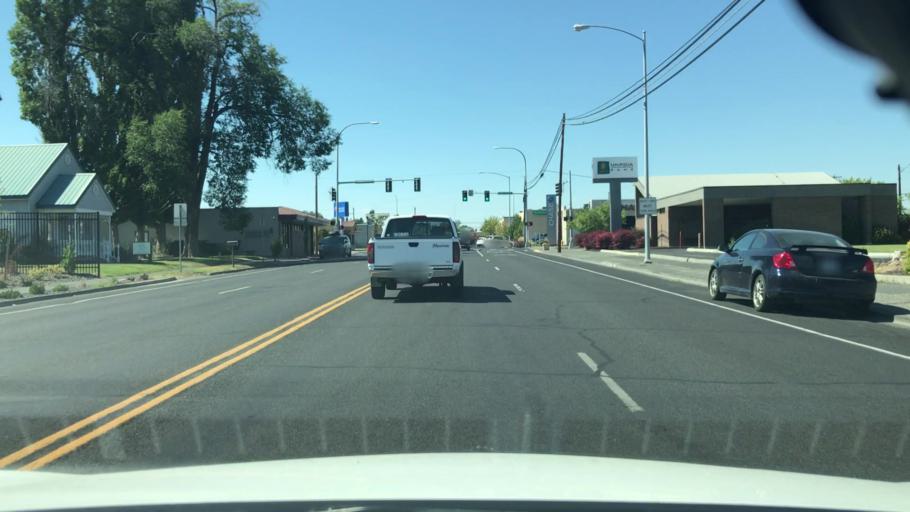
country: US
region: Washington
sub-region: Grant County
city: Moses Lake
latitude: 47.1286
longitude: -119.2765
